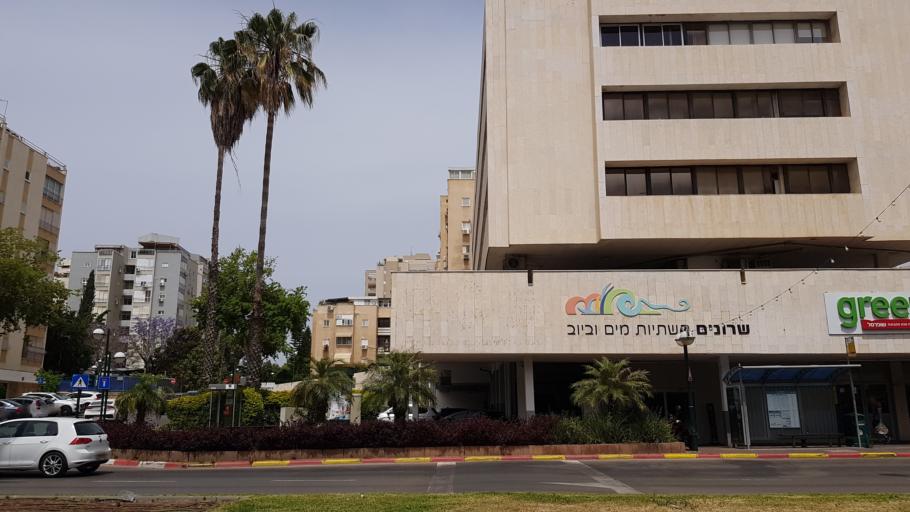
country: IL
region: Tel Aviv
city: Ramat HaSharon
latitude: 32.1382
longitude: 34.8418
